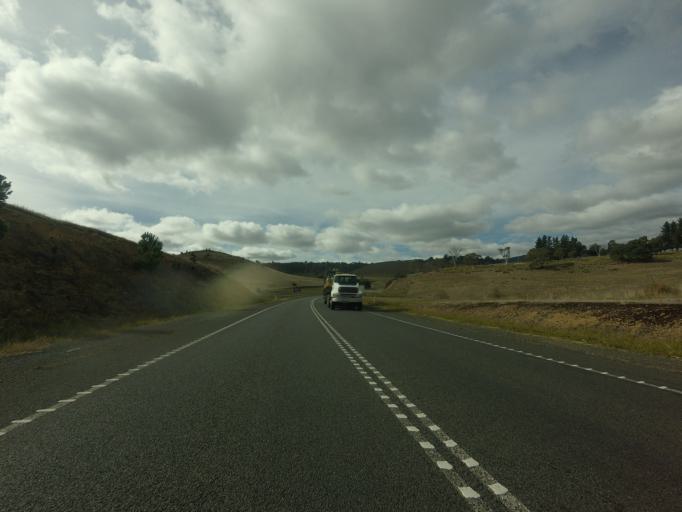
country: AU
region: Tasmania
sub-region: Brighton
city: Bridgewater
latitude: -42.4422
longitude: 147.2293
